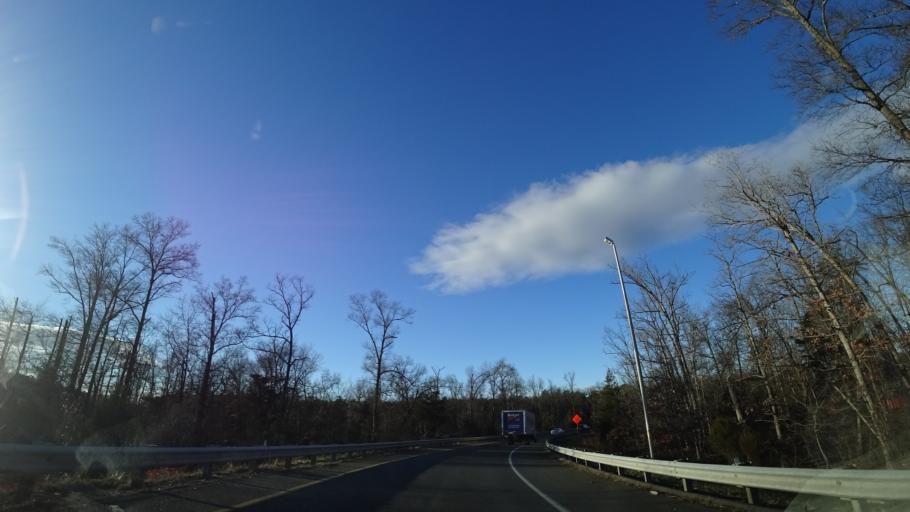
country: US
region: Virginia
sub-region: Prince William County
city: Linton Hall
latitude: 38.7981
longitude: -77.5754
